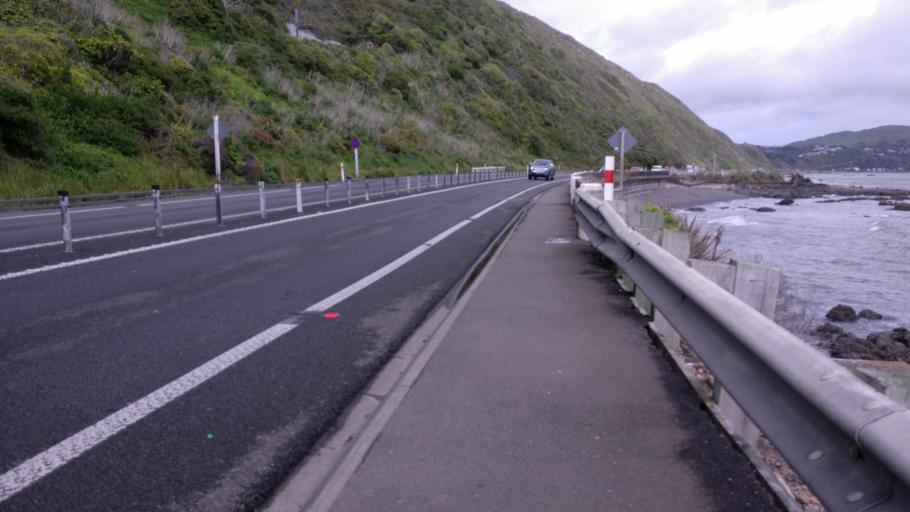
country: NZ
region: Wellington
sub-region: Porirua City
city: Porirua
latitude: -41.0165
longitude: 174.9159
